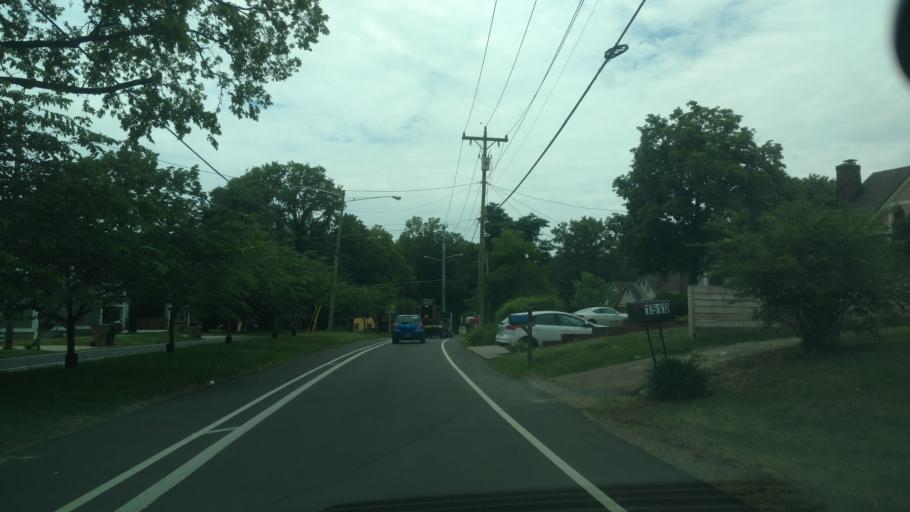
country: US
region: Tennessee
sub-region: Davidson County
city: Nashville
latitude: 36.1939
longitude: -86.7236
